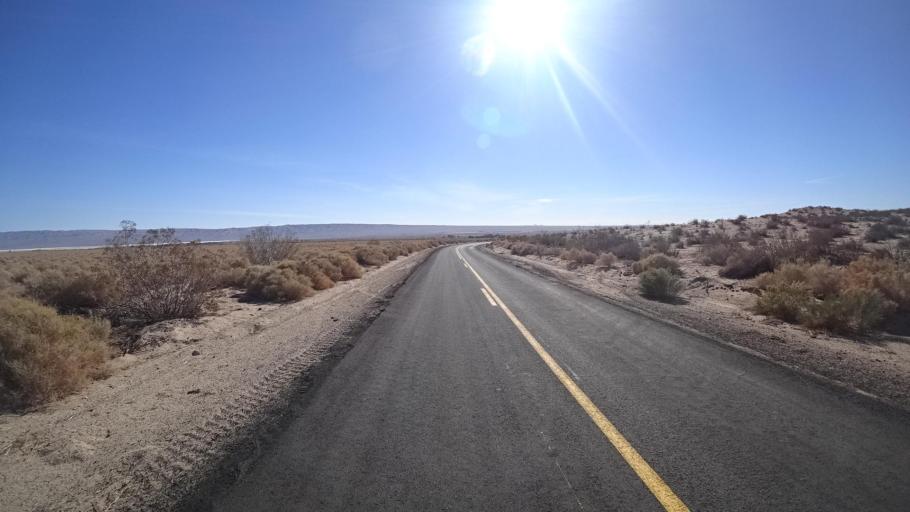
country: US
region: California
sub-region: Kern County
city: California City
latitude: 35.3212
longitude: -117.9617
